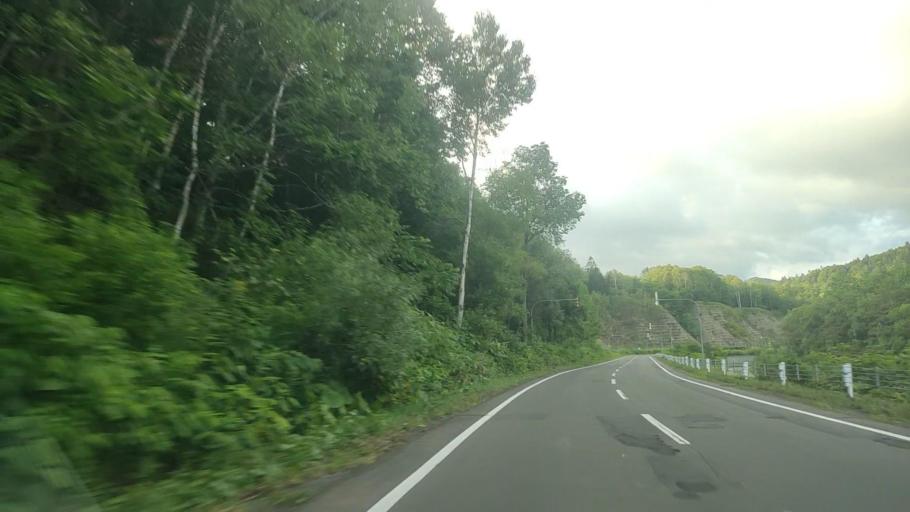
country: JP
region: Hokkaido
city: Bibai
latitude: 43.1174
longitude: 142.0988
